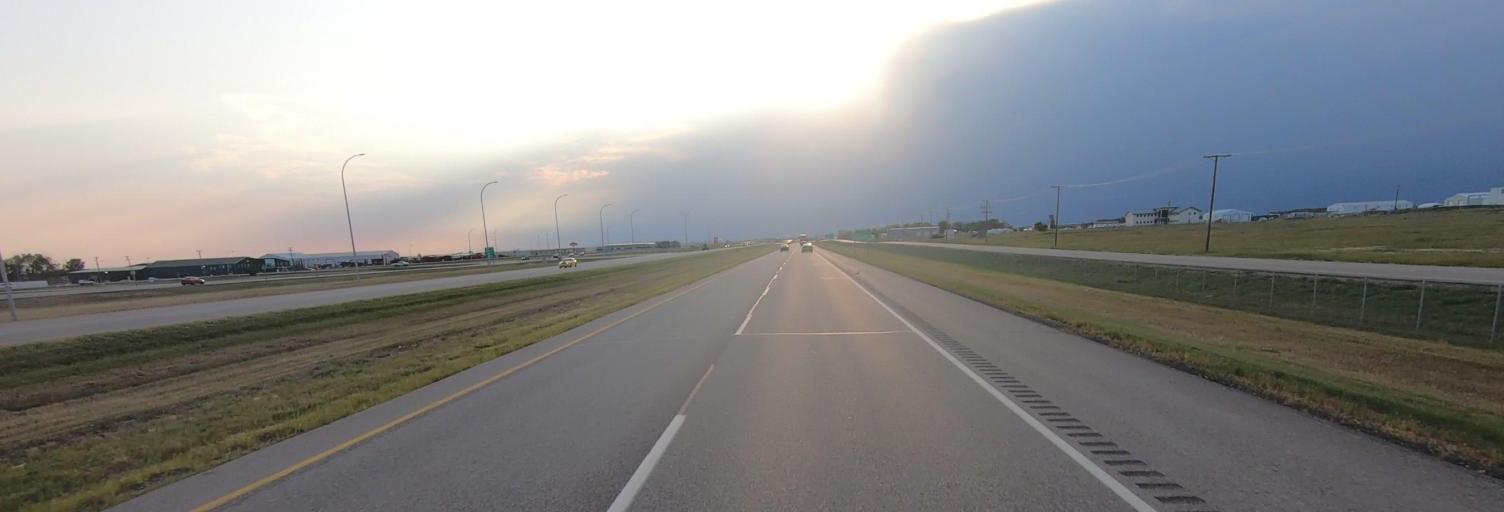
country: CA
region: Saskatchewan
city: Pilot Butte
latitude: 50.4477
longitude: -104.4071
